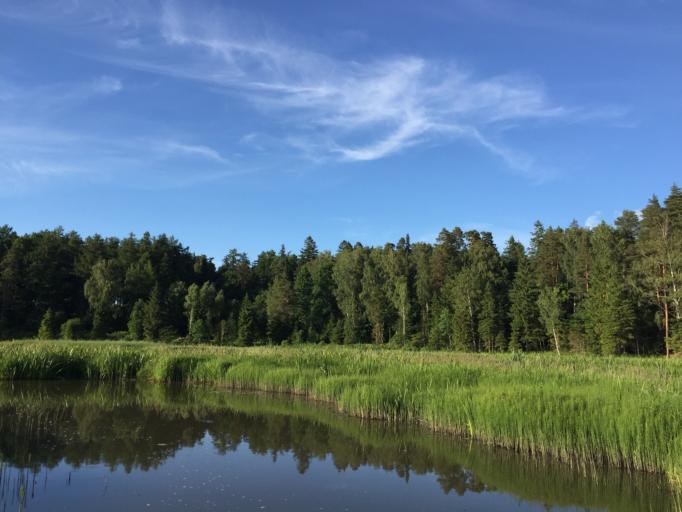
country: LV
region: Aizpute
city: Aizpute
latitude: 56.7243
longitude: 21.7410
